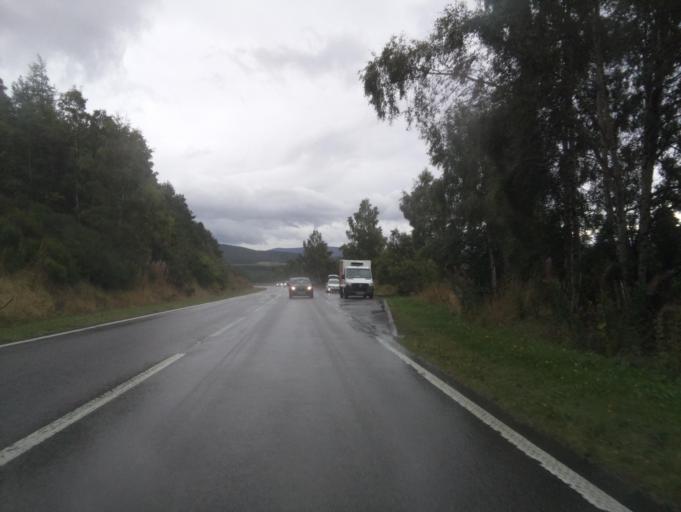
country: GB
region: Scotland
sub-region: Highland
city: Grantown on Spey
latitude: 57.2814
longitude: -3.6787
